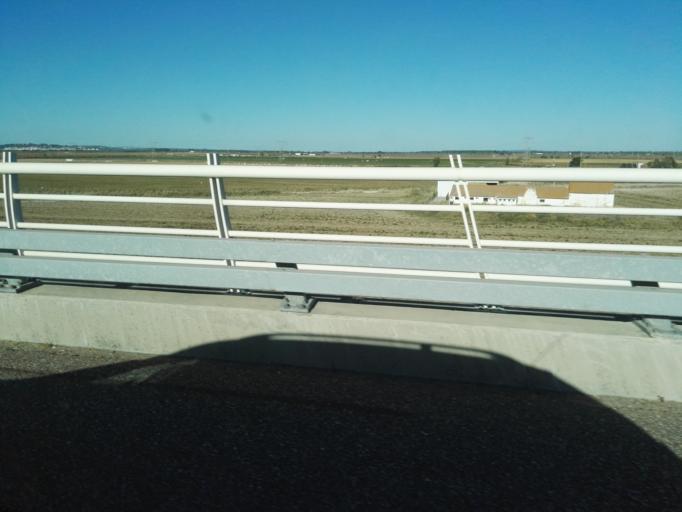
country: PT
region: Santarem
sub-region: Benavente
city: Samora Correia
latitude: 38.9925
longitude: -8.8962
